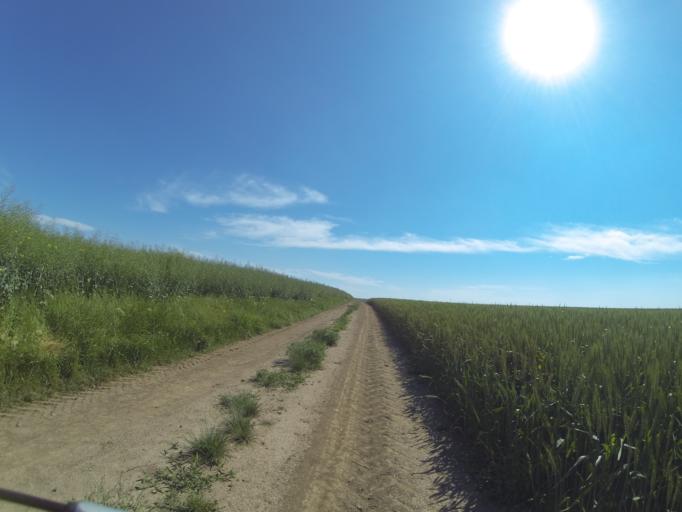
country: RO
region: Dolj
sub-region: Comuna Cosoveni
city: Cosoveni
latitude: 44.2587
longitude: 23.9997
